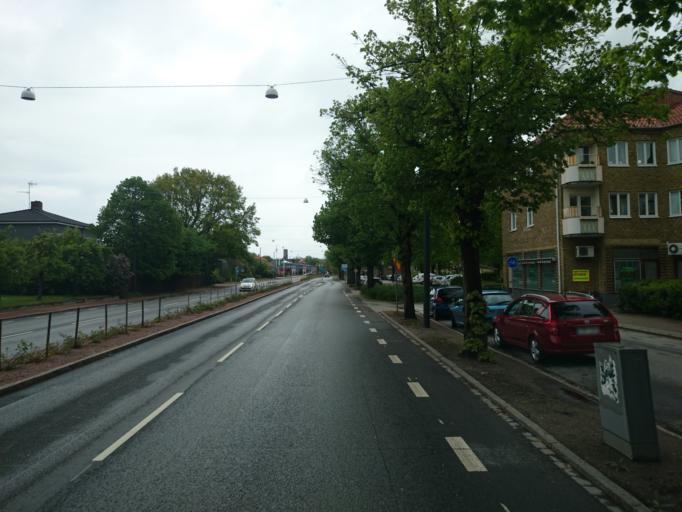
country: SE
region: Skane
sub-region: Malmo
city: Malmoe
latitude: 55.5922
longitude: 12.9635
